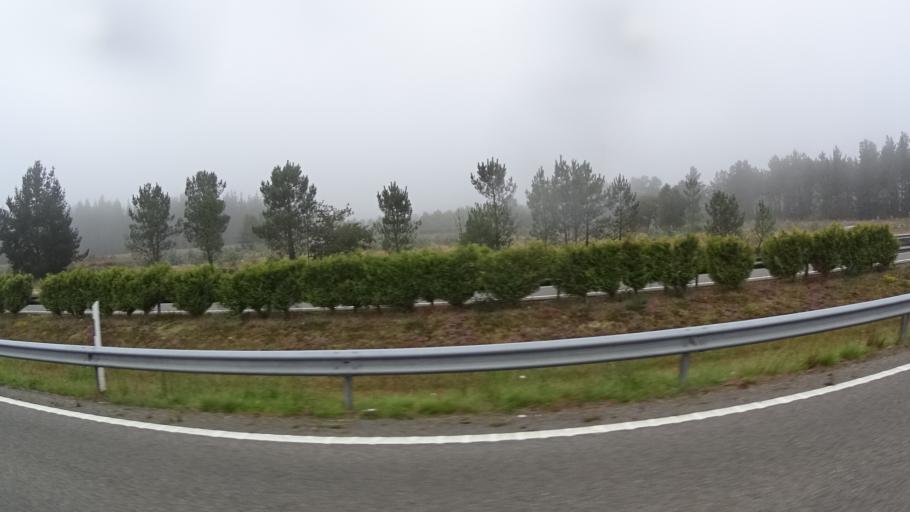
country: ES
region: Galicia
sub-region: Provincia de Lugo
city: Outeiro de Rei
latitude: 43.0892
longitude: -7.5847
